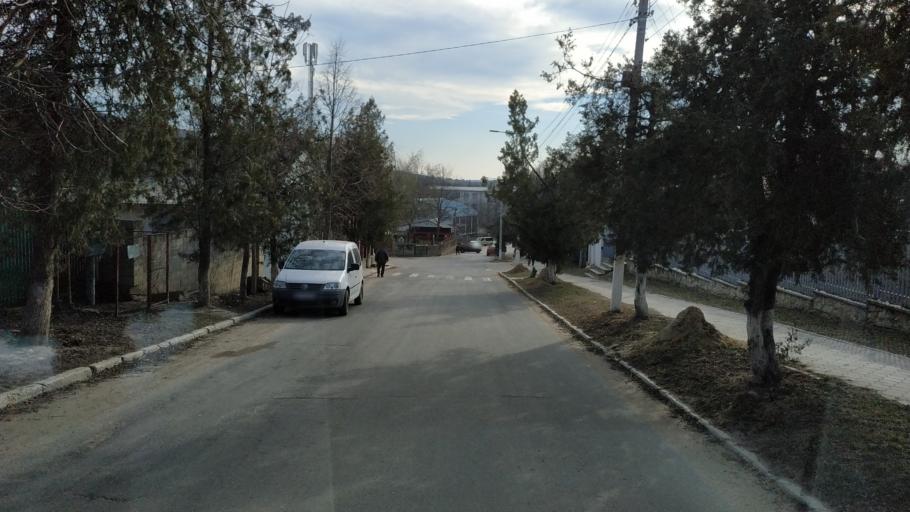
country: MD
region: Nisporeni
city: Nisporeni
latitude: 47.0820
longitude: 28.1882
